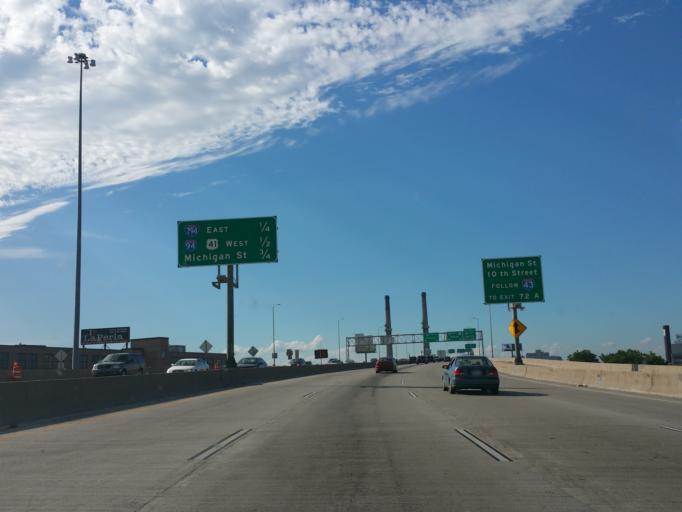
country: US
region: Wisconsin
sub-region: Milwaukee County
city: Milwaukee
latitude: 43.0225
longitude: -87.9205
